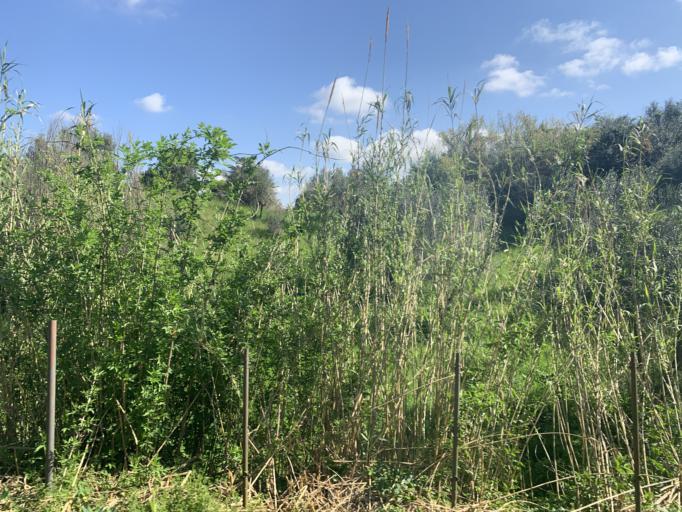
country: IT
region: Latium
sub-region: Citta metropolitana di Roma Capitale
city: Marino
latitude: 41.7785
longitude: 12.6360
